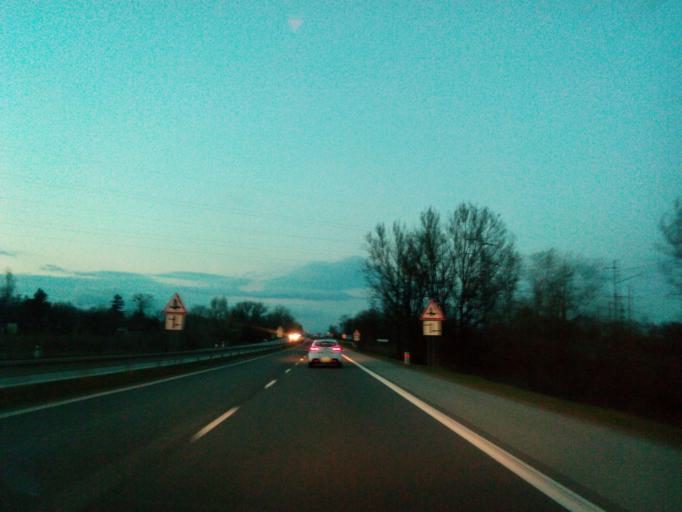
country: SK
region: Kosicky
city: Kosice
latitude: 48.6389
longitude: 21.1996
